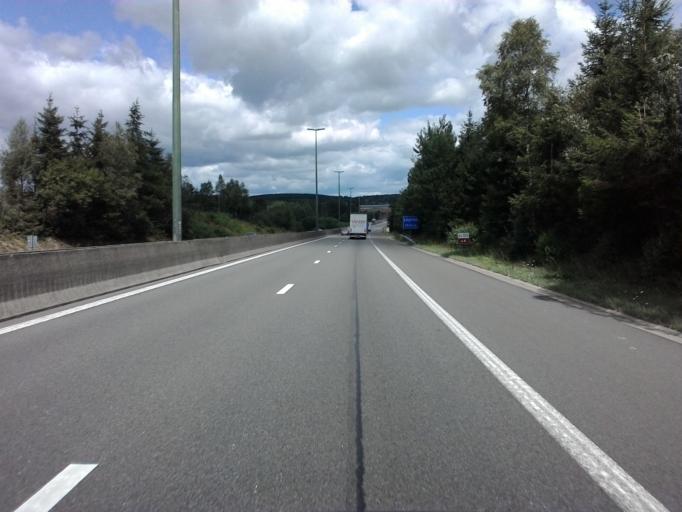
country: BE
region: Wallonia
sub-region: Province du Luxembourg
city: Leglise
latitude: 49.7893
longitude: 5.5296
